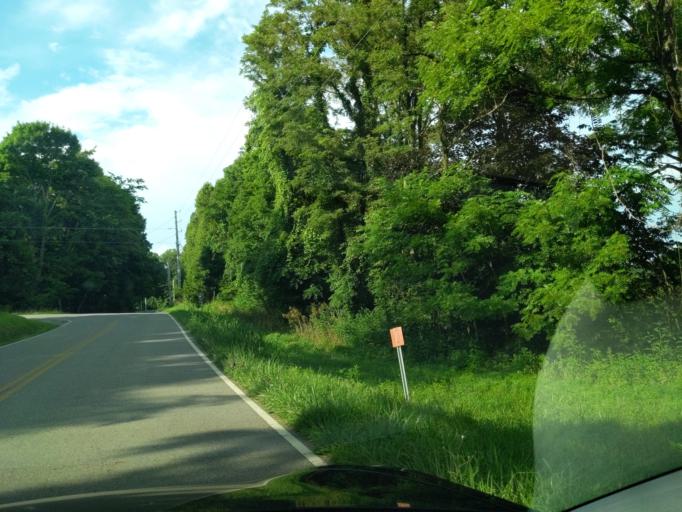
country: US
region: Ohio
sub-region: Fairfield County
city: Lancaster
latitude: 39.5521
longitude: -82.6387
